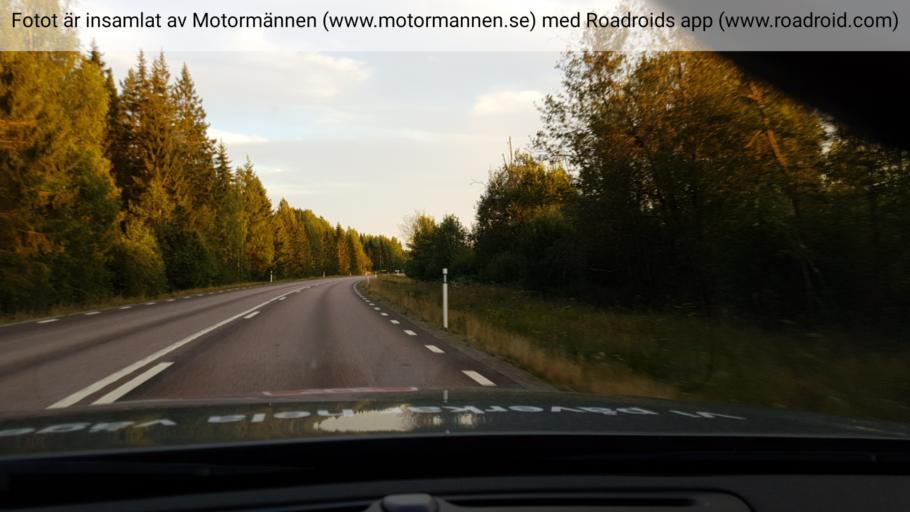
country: SE
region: OErebro
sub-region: Karlskoga Kommun
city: Karlskoga
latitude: 59.4242
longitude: 14.4279
